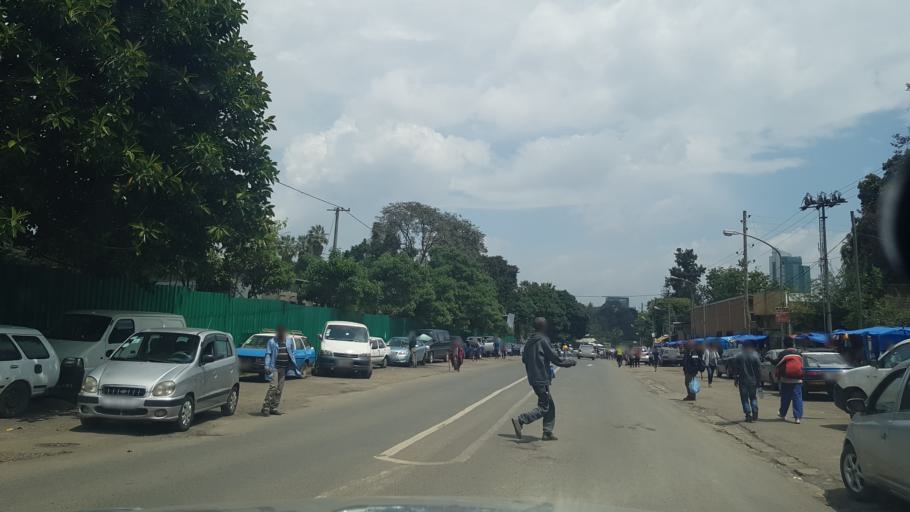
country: ET
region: Adis Abeba
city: Addis Ababa
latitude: 9.0197
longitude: 38.7565
